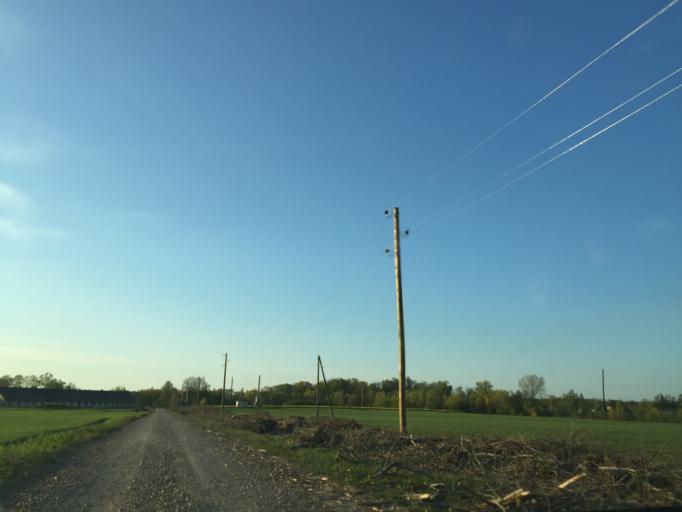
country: LV
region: Bauskas Rajons
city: Bauska
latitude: 56.3131
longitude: 24.1803
